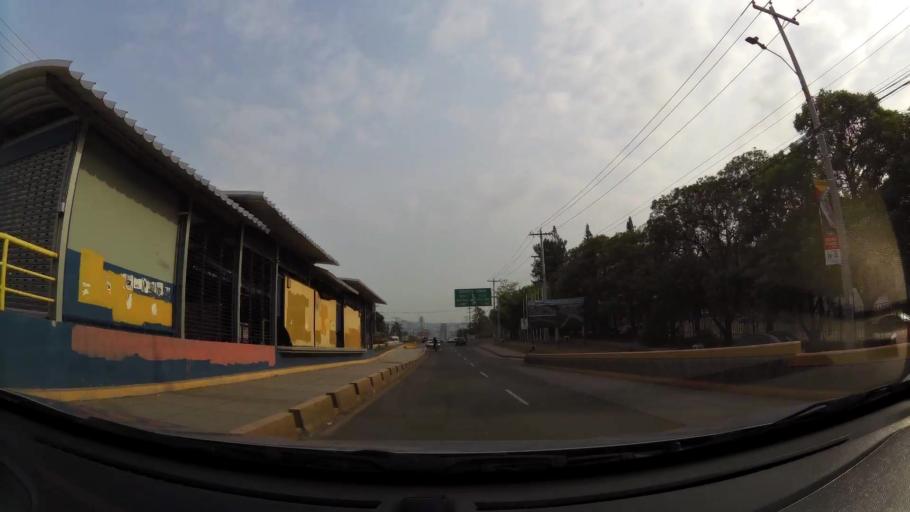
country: HN
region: Francisco Morazan
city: Tegucigalpa
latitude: 14.0726
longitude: -87.1846
